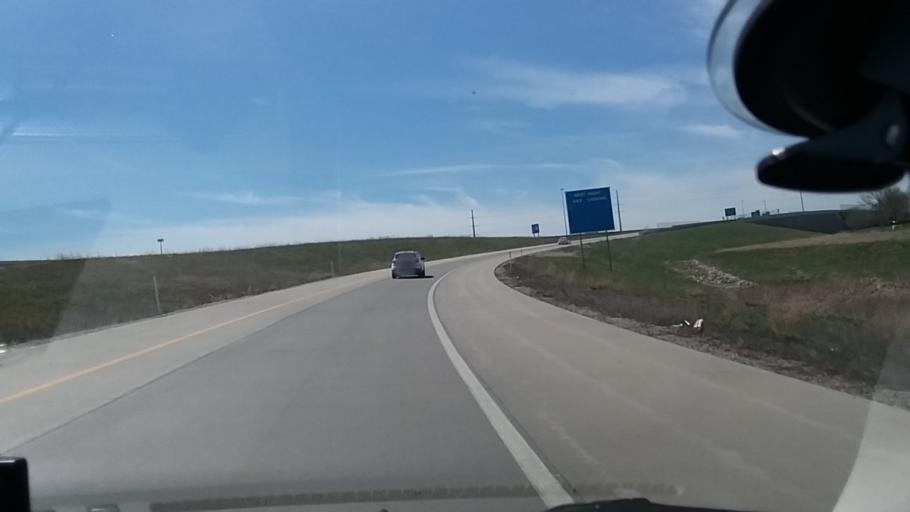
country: US
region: Kansas
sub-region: Johnson County
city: Lenexa
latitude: 38.9416
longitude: -94.7469
